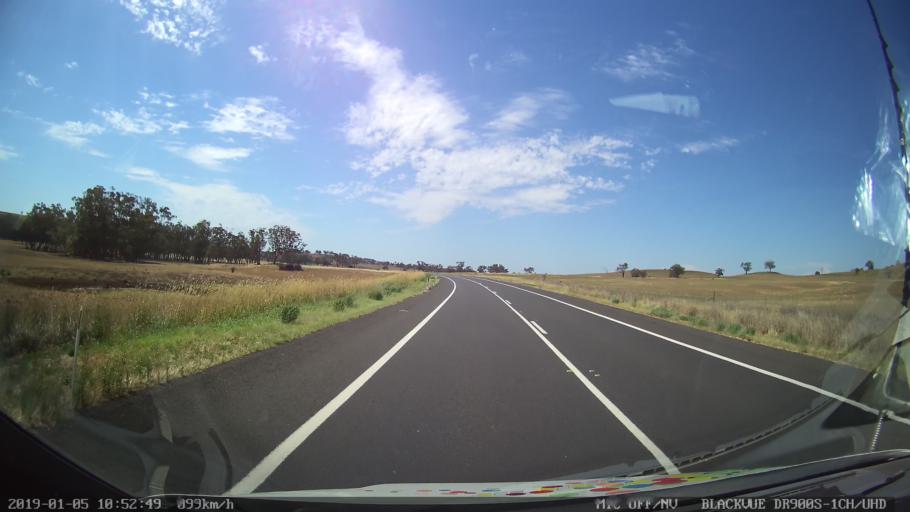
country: AU
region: New South Wales
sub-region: Warrumbungle Shire
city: Coonabarabran
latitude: -31.4367
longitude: 149.1059
